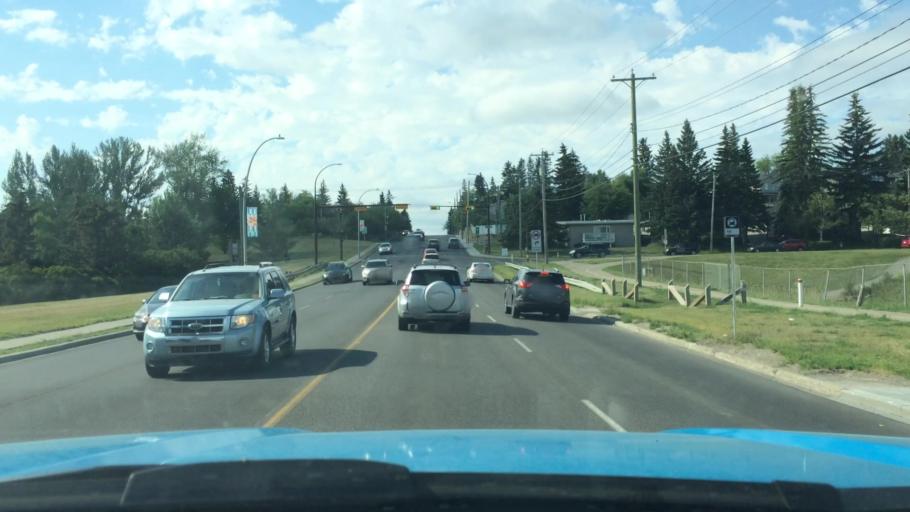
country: CA
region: Alberta
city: Calgary
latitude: 51.0752
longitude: -114.0948
